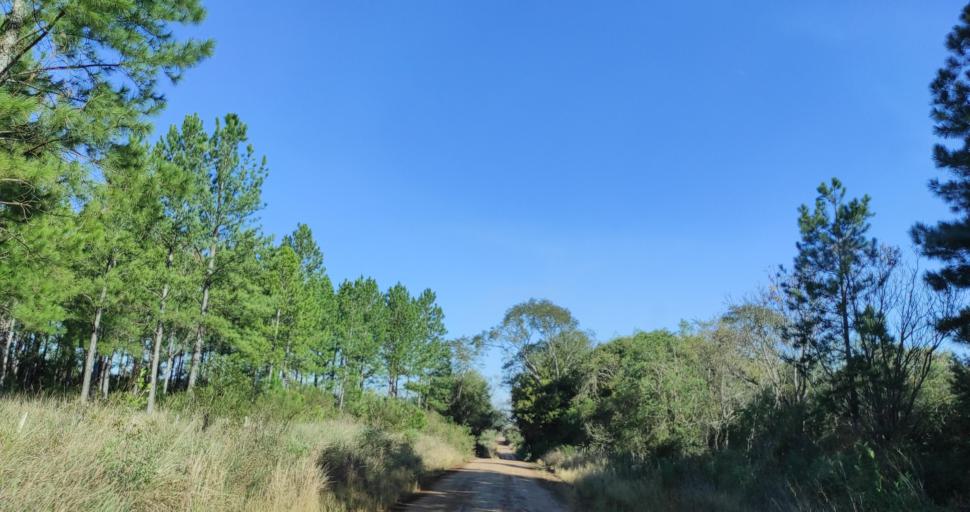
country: AR
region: Misiones
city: Cerro Cora
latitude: -27.6528
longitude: -55.6581
